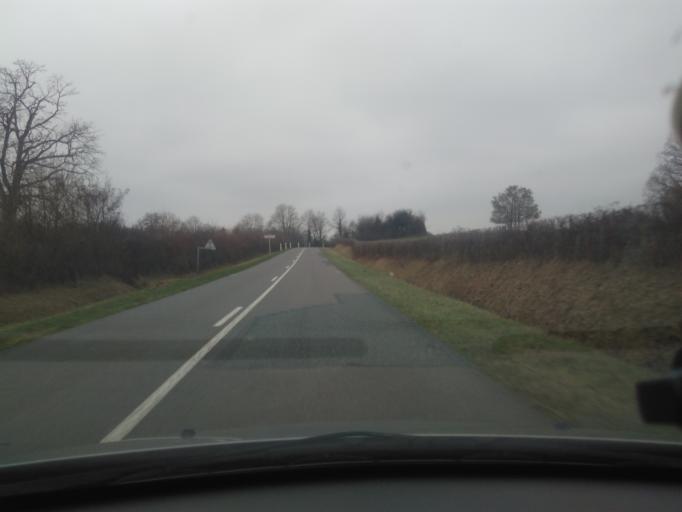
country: FR
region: Centre
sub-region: Departement du Cher
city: Le Chatelet
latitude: 46.6346
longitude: 2.2173
